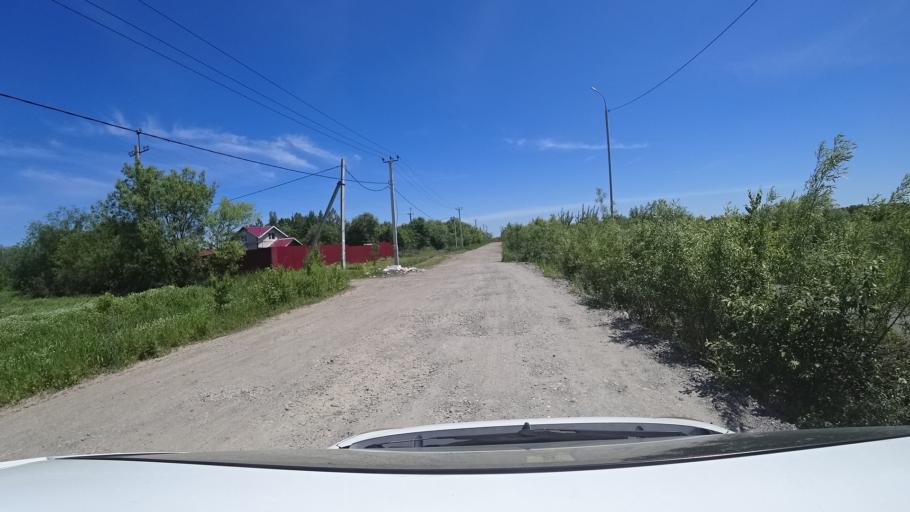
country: RU
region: Khabarovsk Krai
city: Topolevo
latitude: 48.5008
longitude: 135.1921
